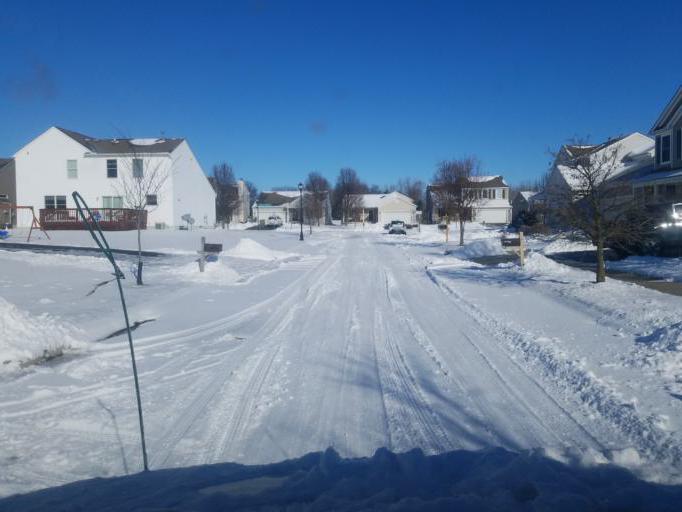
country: US
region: Ohio
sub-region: Franklin County
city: Worthington
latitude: 40.1450
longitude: -83.0137
